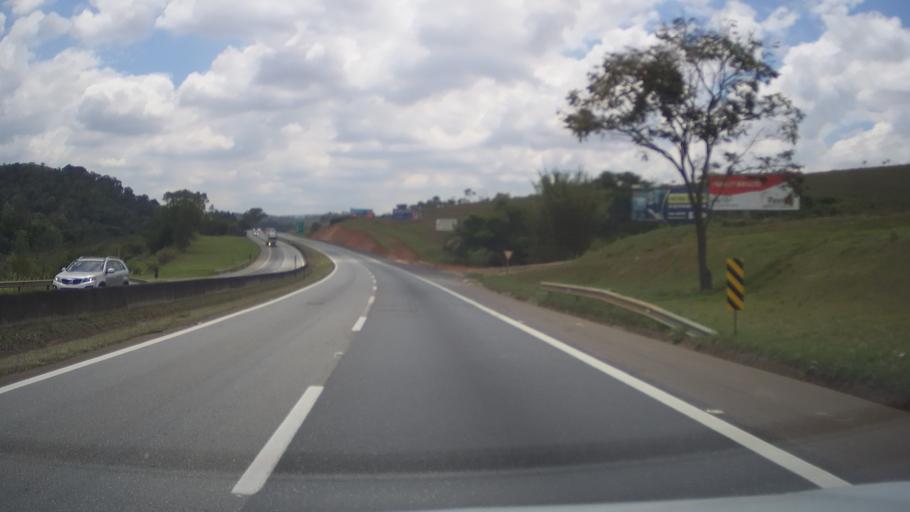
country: BR
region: Minas Gerais
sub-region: Tres Coracoes
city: Tres Coracoes
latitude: -21.6839
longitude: -45.3439
